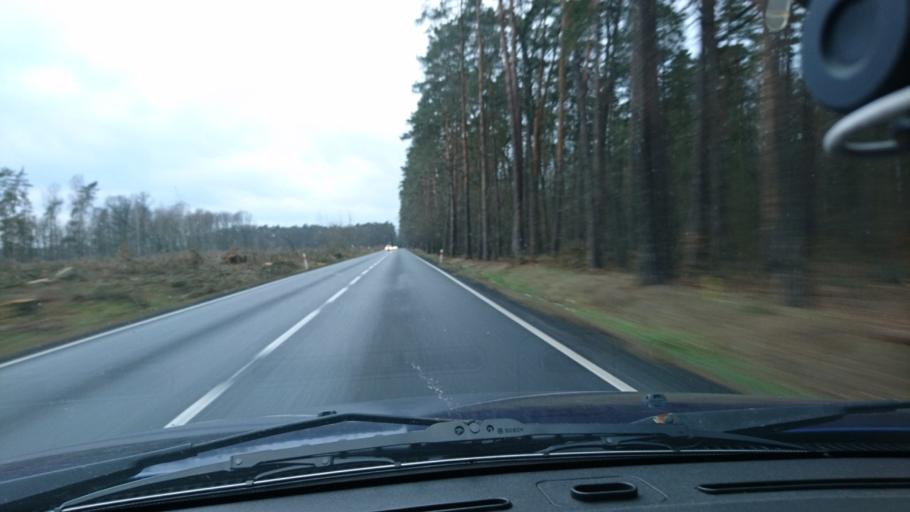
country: PL
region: Opole Voivodeship
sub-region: Powiat oleski
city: Olesno
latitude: 50.9389
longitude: 18.3278
